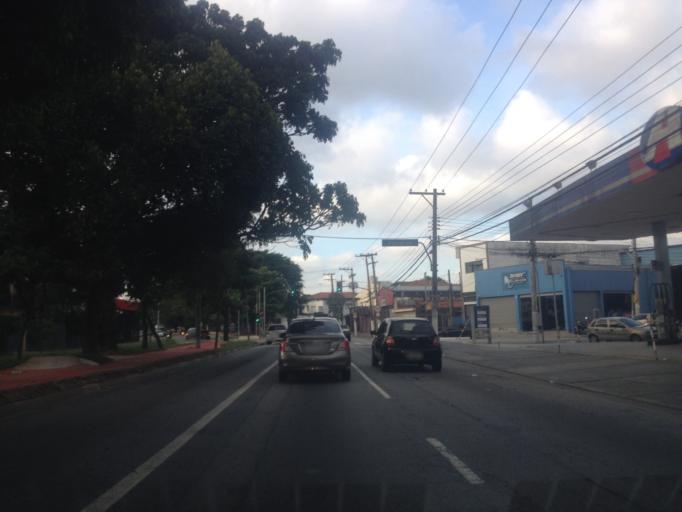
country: BR
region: Sao Paulo
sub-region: Diadema
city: Diadema
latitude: -23.6798
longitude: -46.7128
